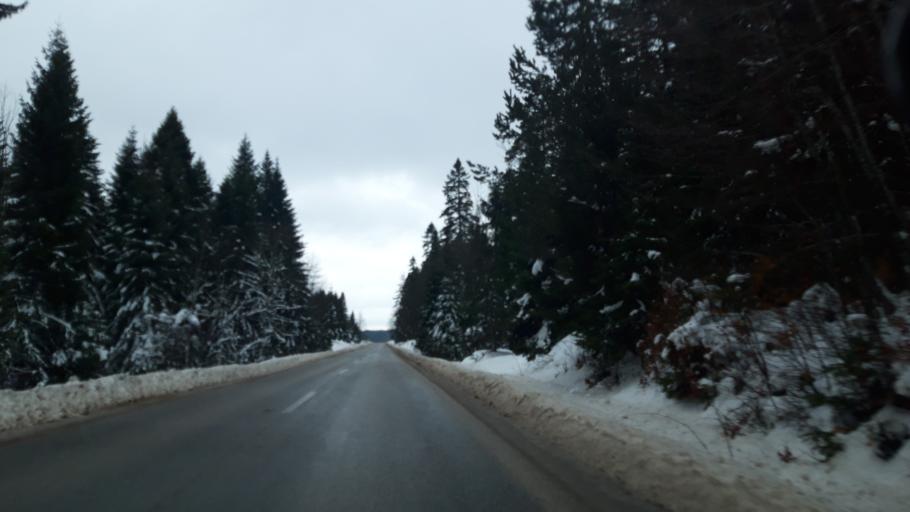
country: BA
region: Republika Srpska
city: Han Pijesak
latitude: 44.0653
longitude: 18.9453
